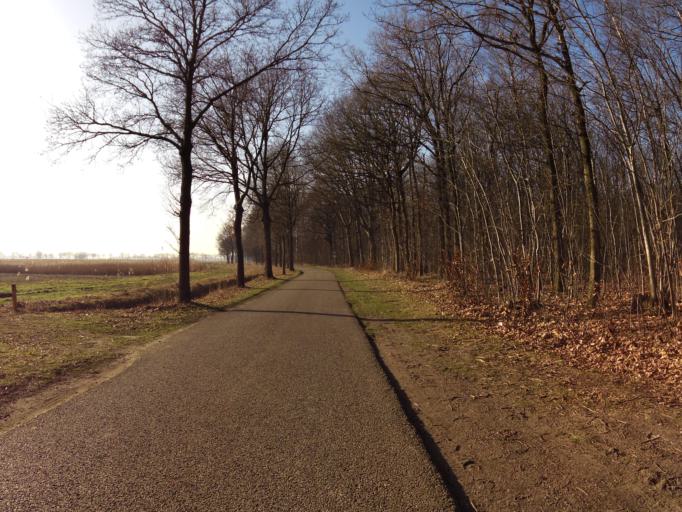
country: NL
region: North Brabant
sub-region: Gemeente Heusden
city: Heusden
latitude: 51.6851
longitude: 5.1926
